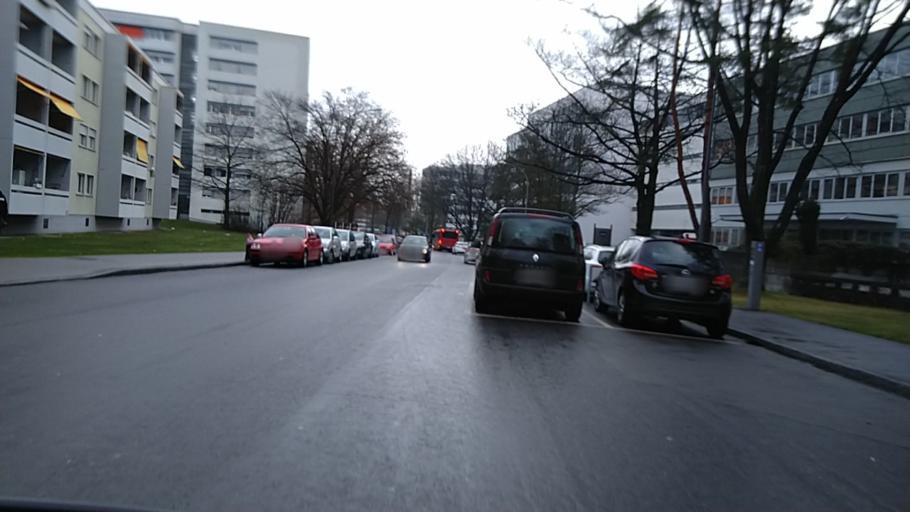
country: CH
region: Bern
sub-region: Bern-Mittelland District
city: Koniz
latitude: 46.9468
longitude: 7.3861
